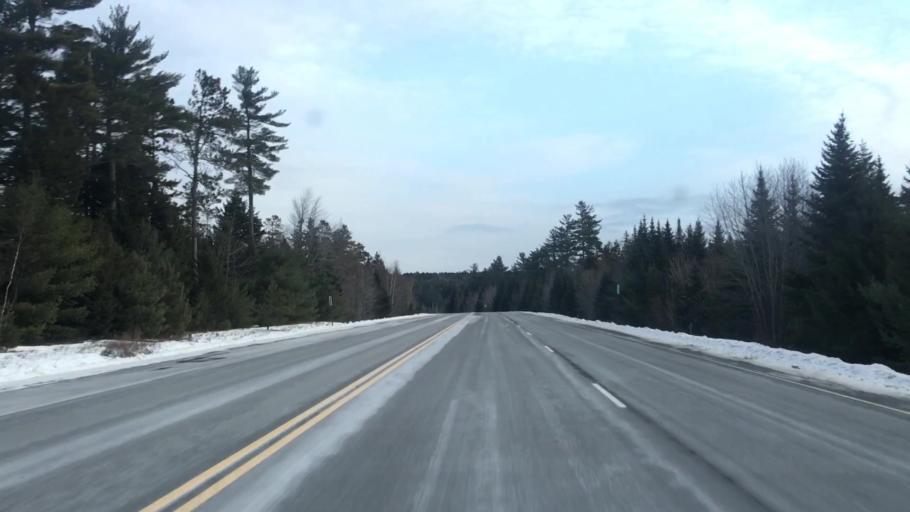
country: US
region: Maine
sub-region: Washington County
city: Addison
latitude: 44.9132
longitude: -67.7932
